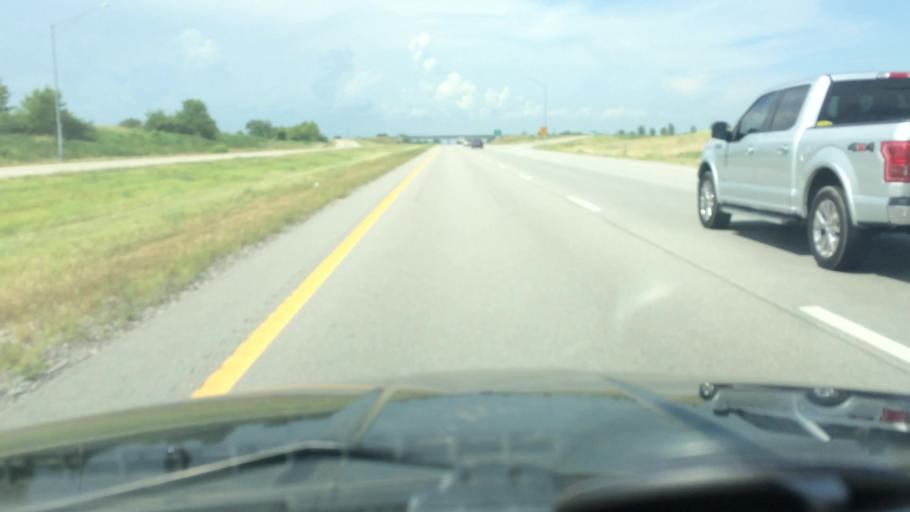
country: US
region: Missouri
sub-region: Henry County
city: Clinton
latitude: 38.2442
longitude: -93.7619
